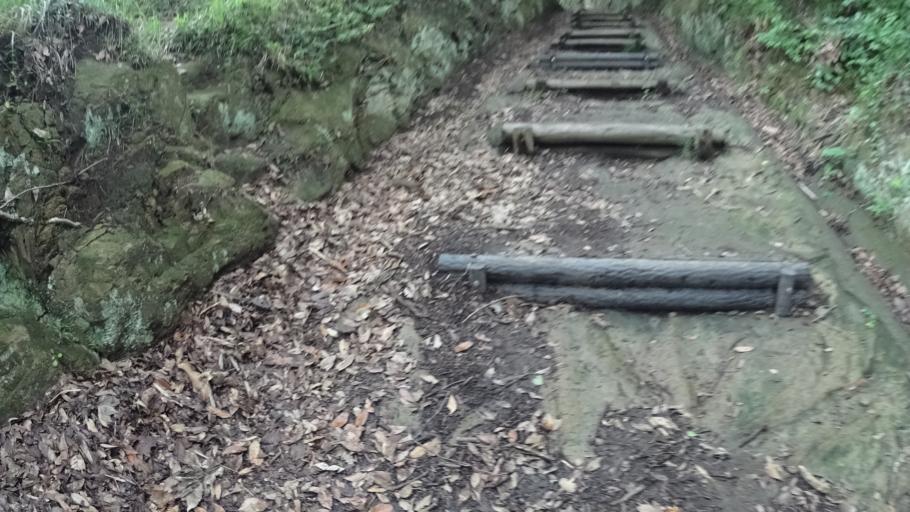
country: JP
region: Kanagawa
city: Zushi
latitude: 35.3473
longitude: 139.6215
